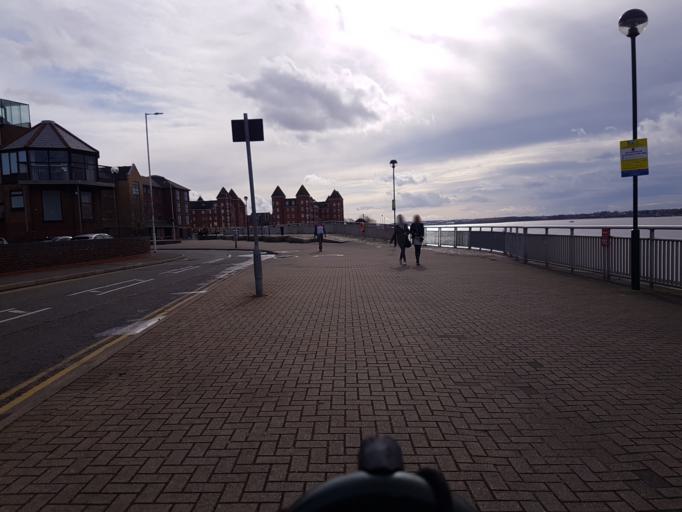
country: GB
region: England
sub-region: Liverpool
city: Liverpool
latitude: 53.3919
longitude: -2.9889
